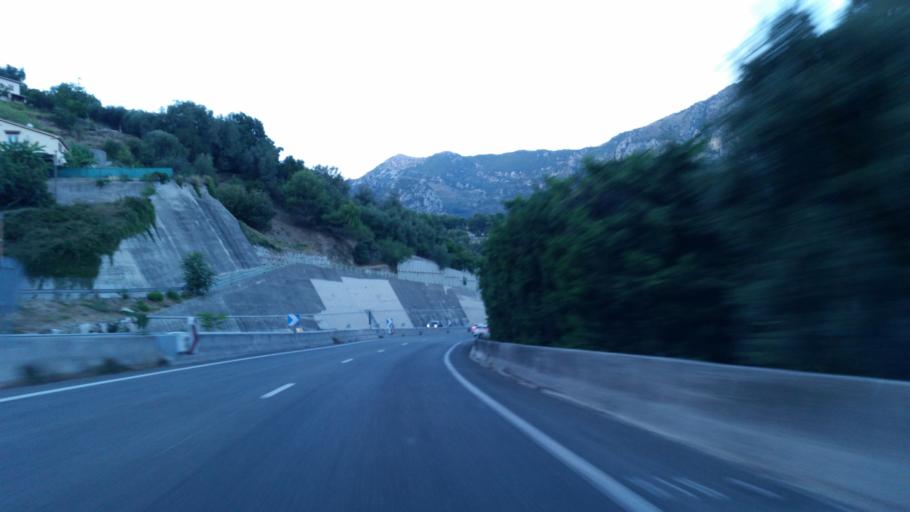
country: FR
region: Provence-Alpes-Cote d'Azur
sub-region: Departement des Alpes-Maritimes
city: Sainte-Agnes
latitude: 43.7946
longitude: 7.4759
